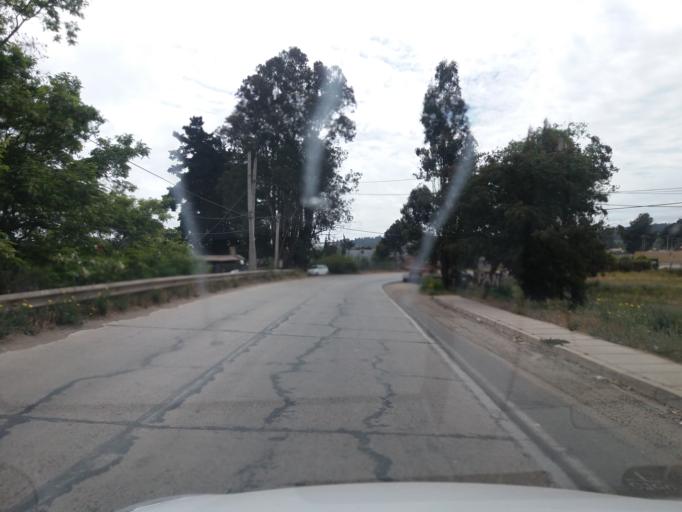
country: CL
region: Valparaiso
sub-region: Provincia de Marga Marga
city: Quilpue
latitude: -32.9314
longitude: -71.4391
